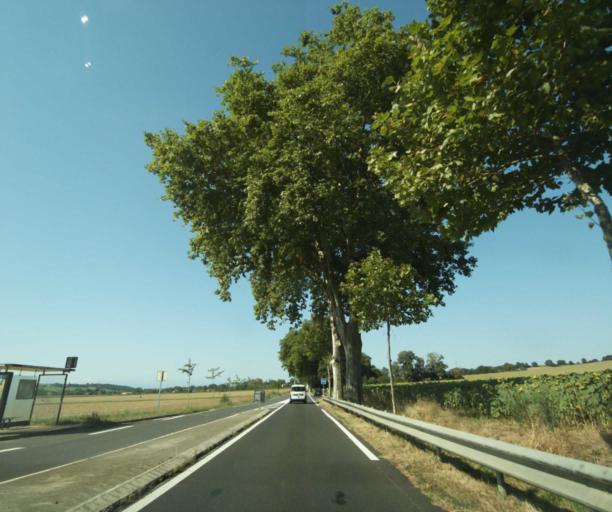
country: FR
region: Midi-Pyrenees
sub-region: Departement de la Haute-Garonne
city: Beaumont-sur-Leze
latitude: 43.3942
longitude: 1.3573
